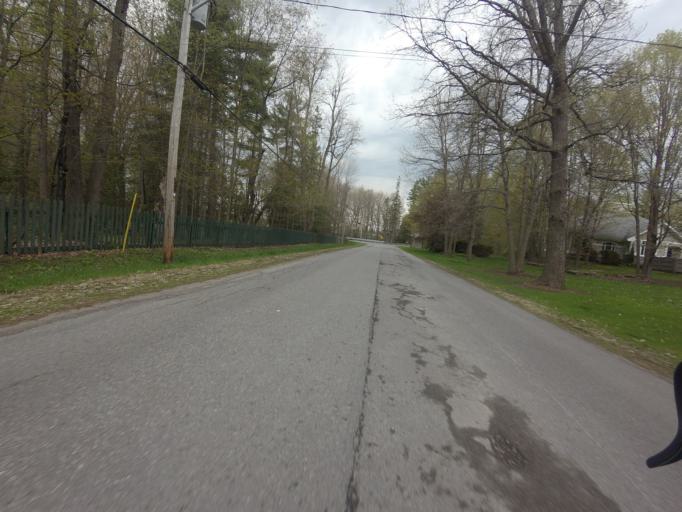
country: CA
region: Ontario
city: Carleton Place
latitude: 45.2267
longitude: -76.2051
